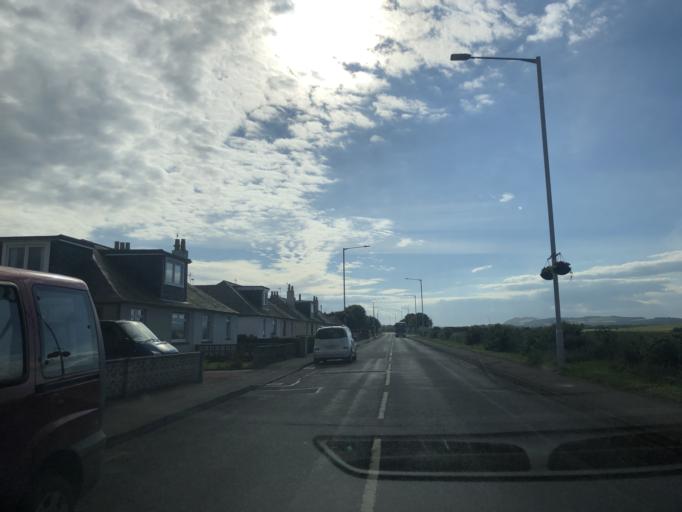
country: GB
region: Scotland
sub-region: Fife
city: Saint Monance
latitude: 56.2079
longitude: -2.7643
